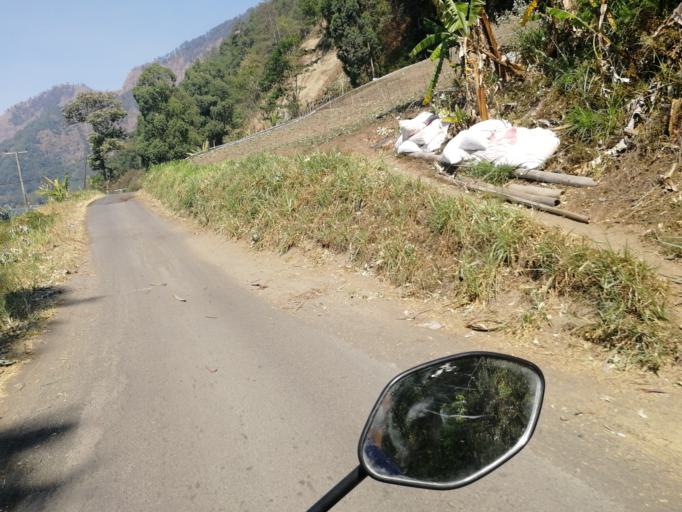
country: ID
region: Bali
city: Banjar Buahan
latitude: -8.2872
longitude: 115.3973
